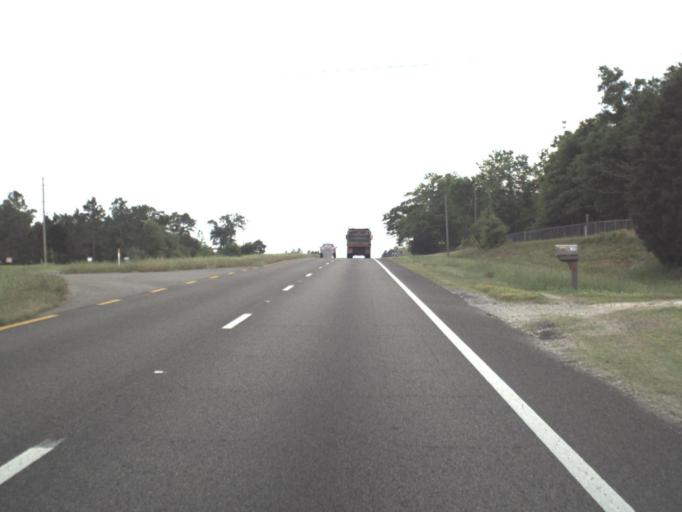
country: US
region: Florida
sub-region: Escambia County
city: Molino
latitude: 30.7124
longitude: -87.3501
